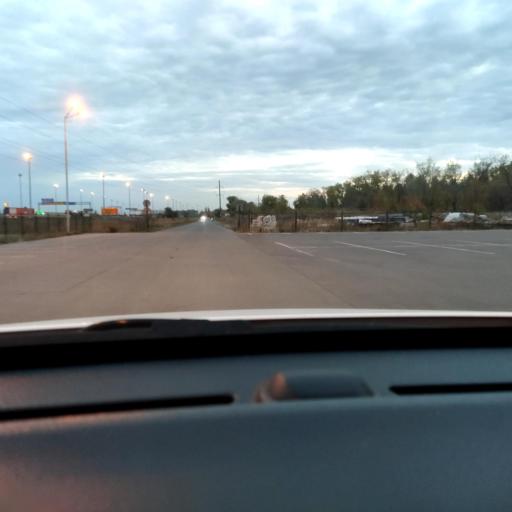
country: RU
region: Voronezj
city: Somovo
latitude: 51.6609
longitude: 39.3010
